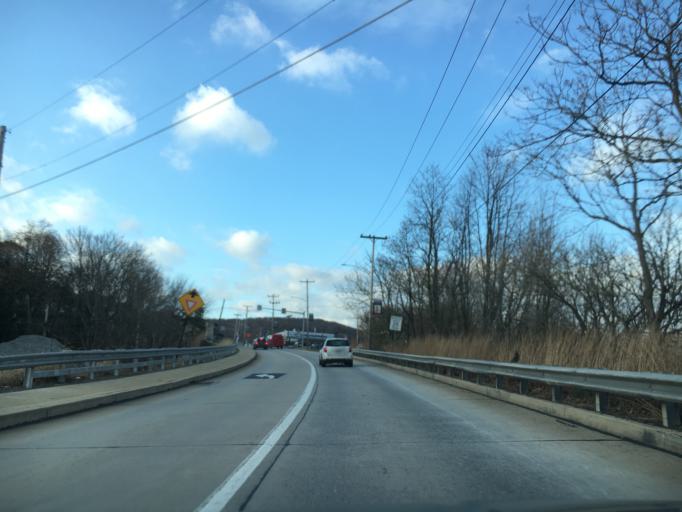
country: US
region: Pennsylvania
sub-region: Carbon County
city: Lehighton
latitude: 40.8369
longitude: -75.7079
